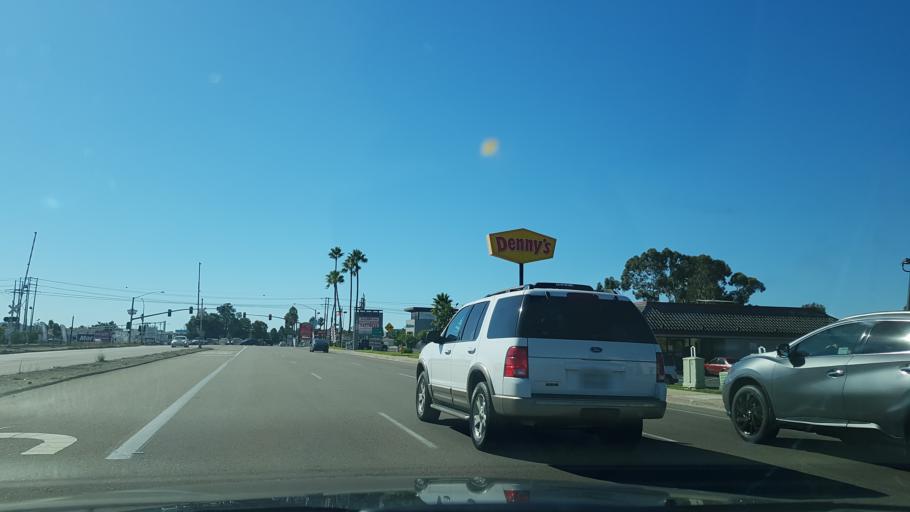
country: US
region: California
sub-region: San Diego County
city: La Jolla
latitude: 32.8785
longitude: -117.1664
